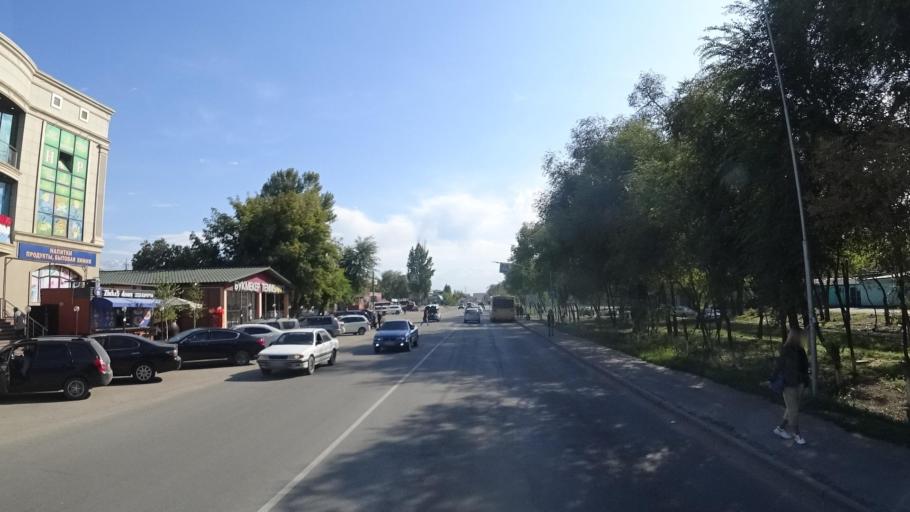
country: KZ
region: Almaty Oblysy
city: Energeticheskiy
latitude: 43.4169
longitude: 77.0212
